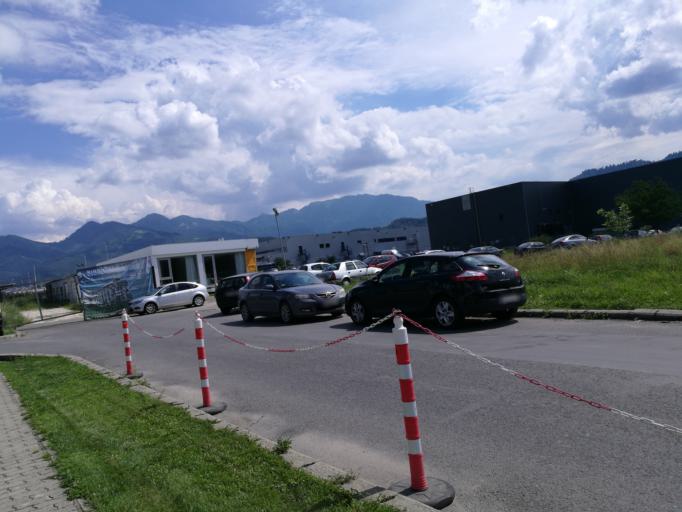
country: RO
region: Brasov
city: Brasov
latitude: 45.6345
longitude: 25.6392
